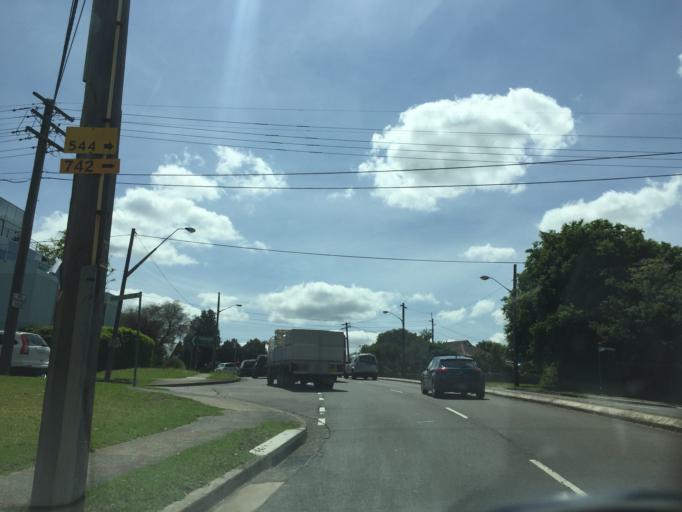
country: AU
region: New South Wales
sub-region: Ryde
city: Denistone
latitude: -33.7915
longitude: 151.0864
